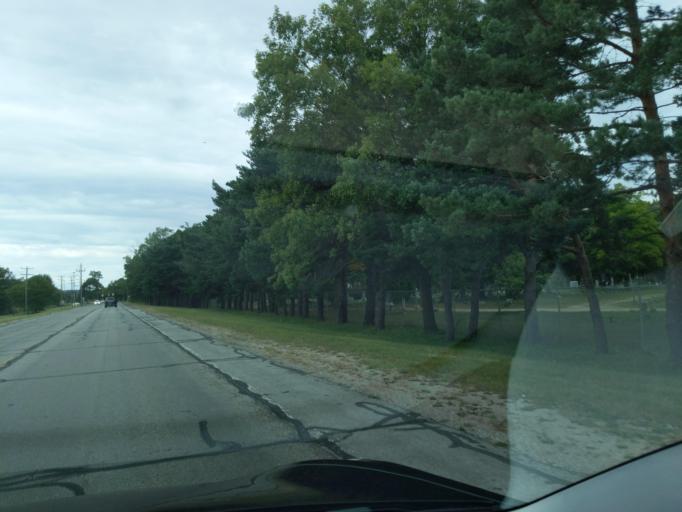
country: US
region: Michigan
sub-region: Grand Traverse County
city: Traverse City
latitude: 44.7536
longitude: -85.5881
